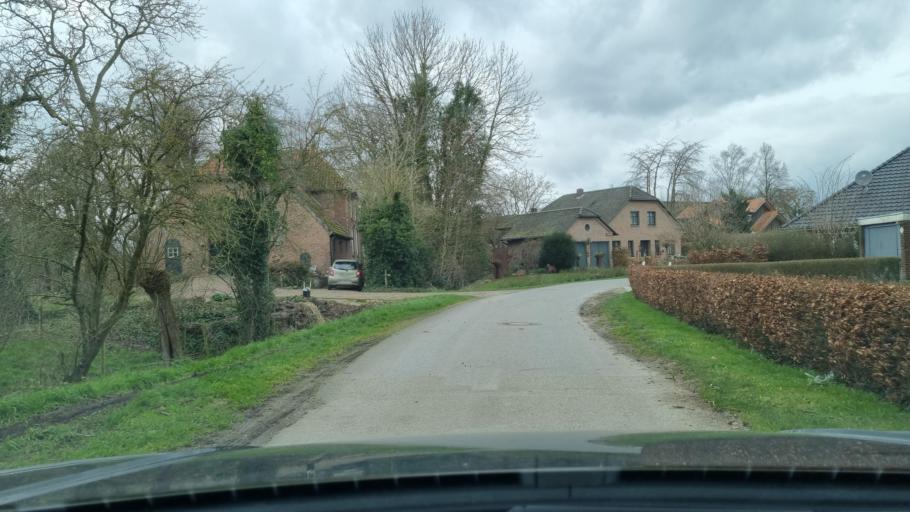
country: DE
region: North Rhine-Westphalia
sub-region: Regierungsbezirk Dusseldorf
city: Kleve
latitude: 51.8424
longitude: 6.0797
